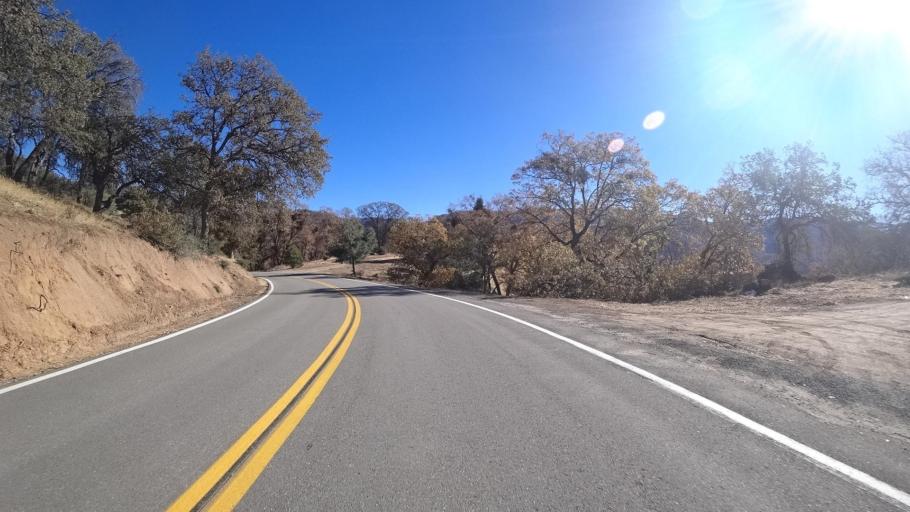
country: US
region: California
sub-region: Kern County
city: Alta Sierra
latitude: 35.7426
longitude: -118.6039
